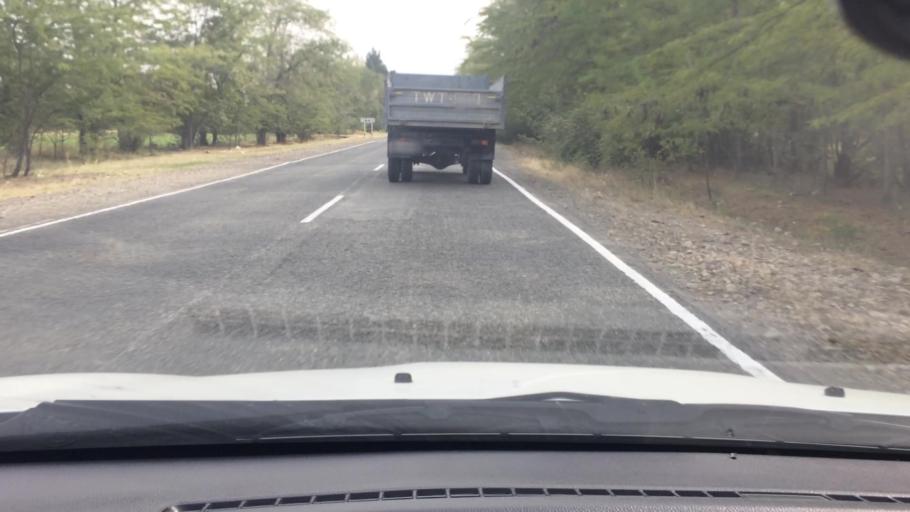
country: GE
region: Kvemo Kartli
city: Rust'avi
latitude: 41.4716
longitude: 44.9786
